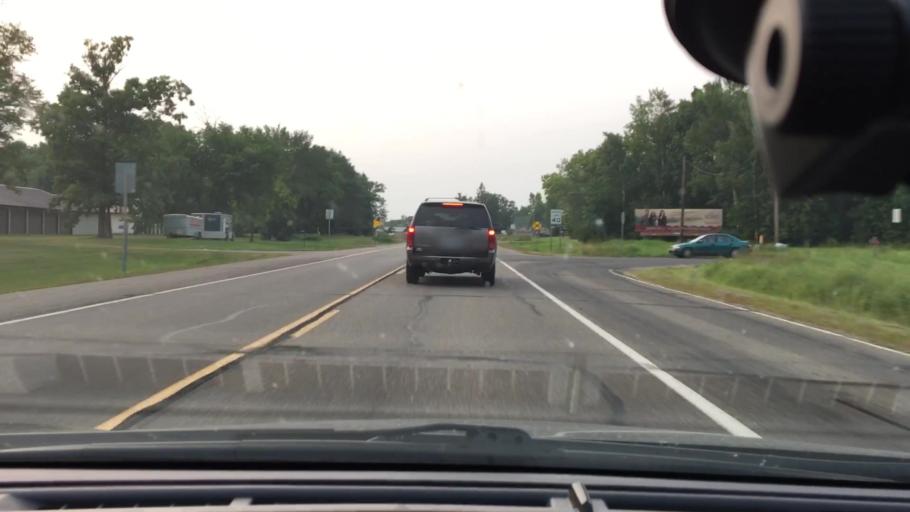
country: US
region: Minnesota
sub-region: Crow Wing County
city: Crosby
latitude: 46.4715
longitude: -93.8895
